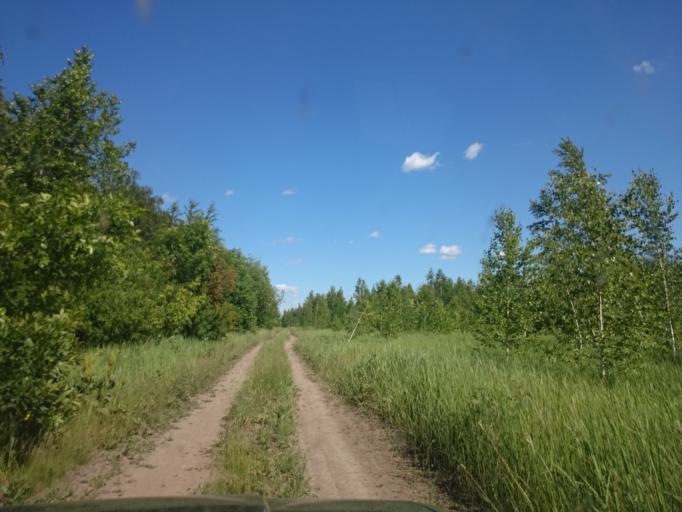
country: RU
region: Mordoviya
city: Kadoshkino
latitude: 54.0524
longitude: 44.4904
